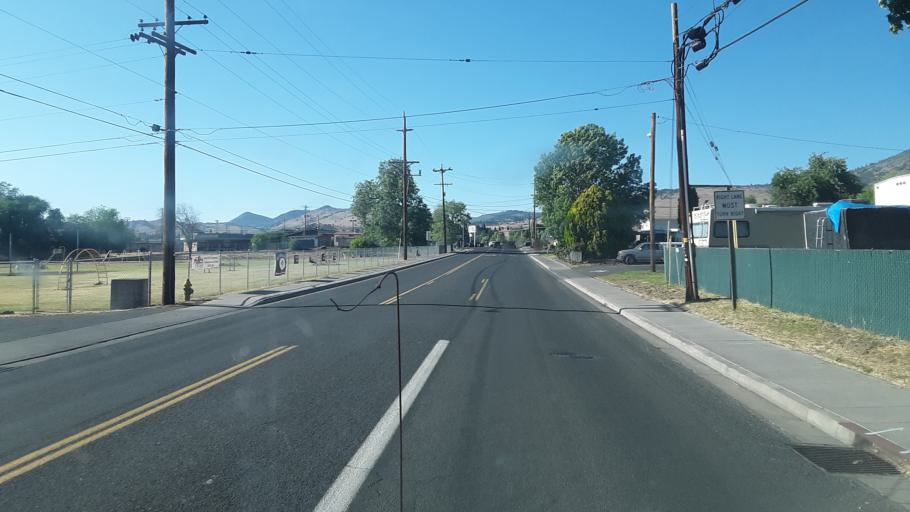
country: US
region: Oregon
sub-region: Klamath County
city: Altamont
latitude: 42.2045
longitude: -121.7378
